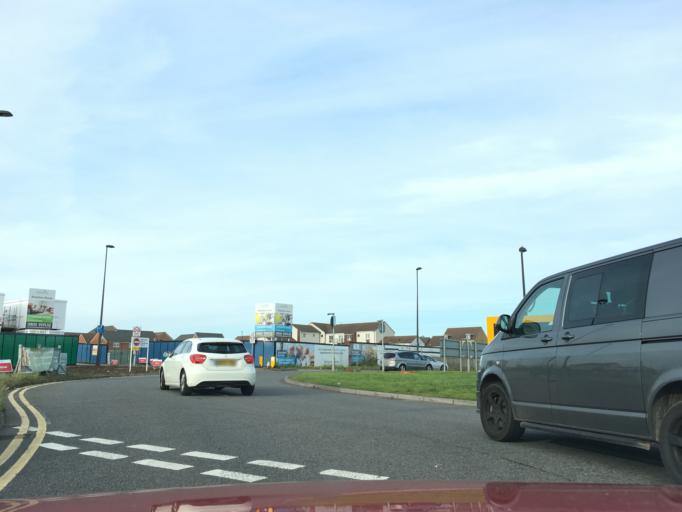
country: GB
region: England
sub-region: South Gloucestershire
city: Almondsbury
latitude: 51.5260
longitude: -2.5754
